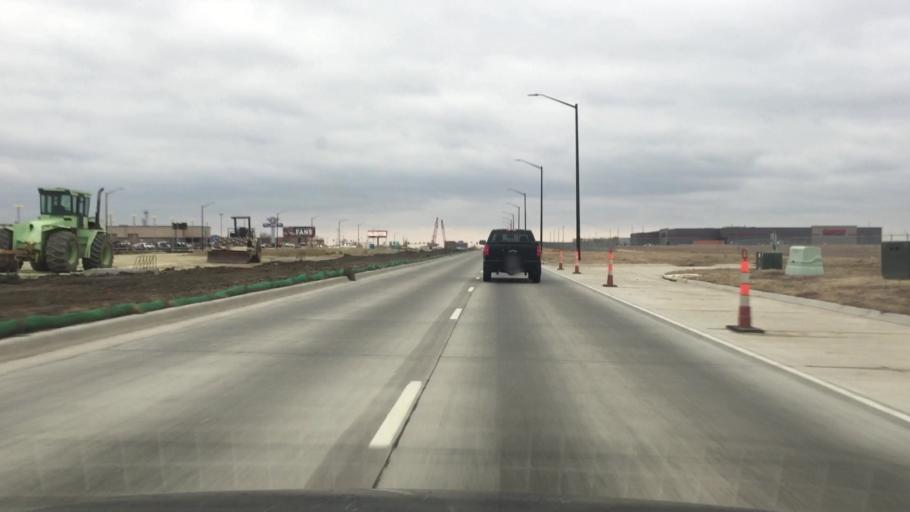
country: US
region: Kansas
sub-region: Butler County
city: Andover
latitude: 37.6794
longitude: -97.2170
